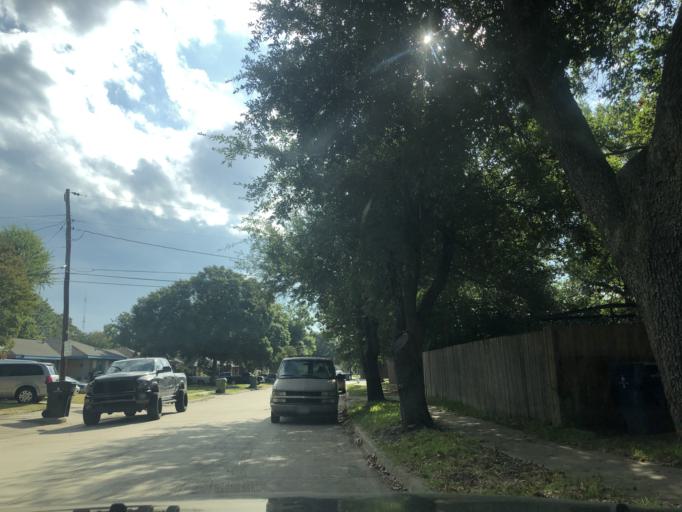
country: US
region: Texas
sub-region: Dallas County
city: Garland
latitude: 32.8888
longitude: -96.6572
